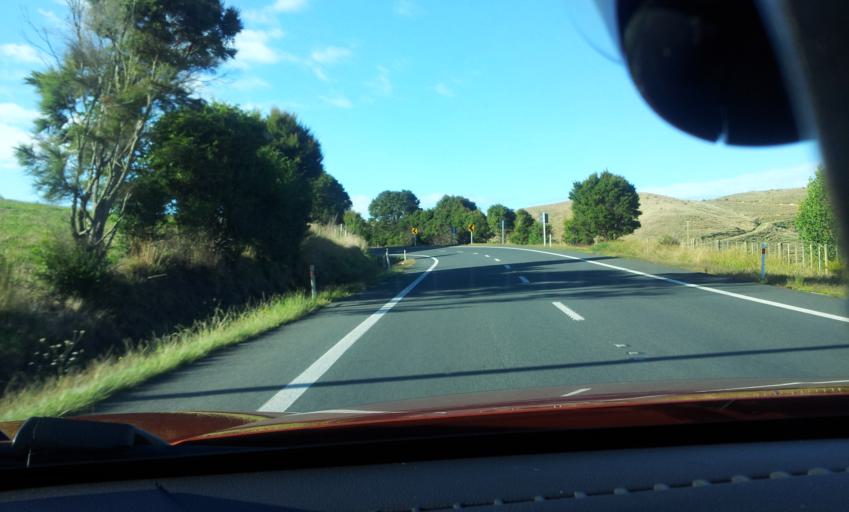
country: NZ
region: Waikato
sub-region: Hauraki District
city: Ngatea
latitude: -37.3506
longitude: 175.4126
